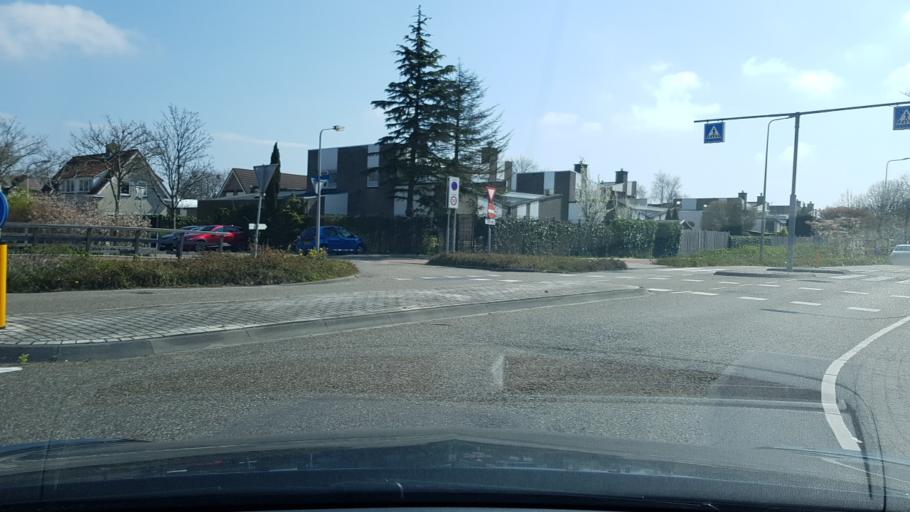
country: NL
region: South Holland
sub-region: Gemeente Teylingen
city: Voorhout
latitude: 52.2237
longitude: 4.4888
